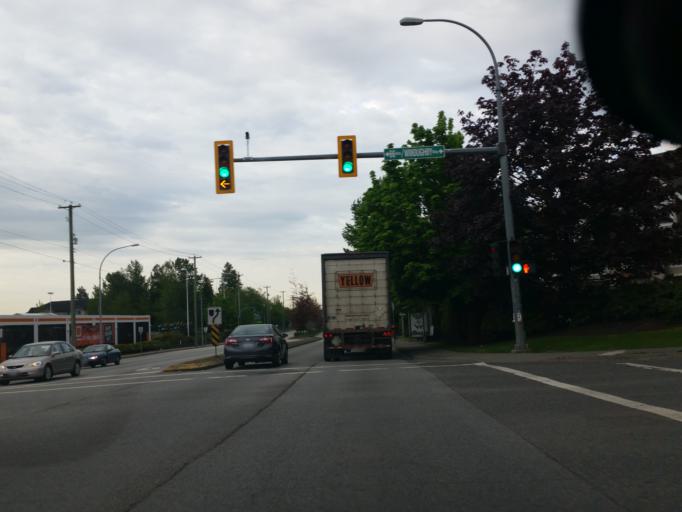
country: CA
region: British Columbia
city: Langley
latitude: 49.1228
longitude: -122.6688
